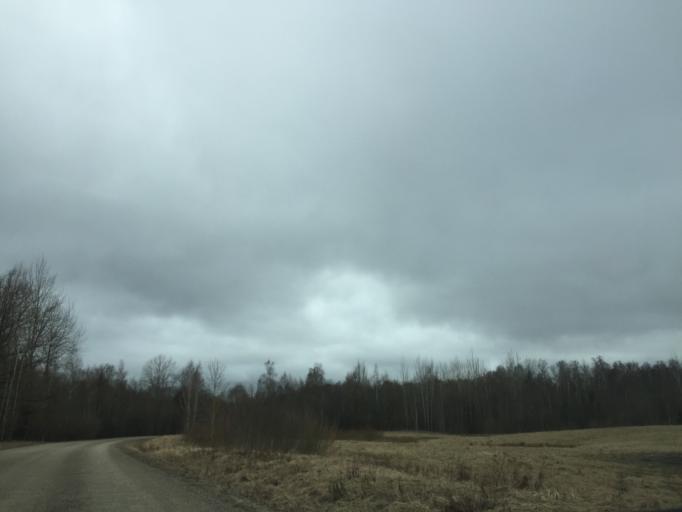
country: LV
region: Ilukste
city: Ilukste
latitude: 56.0225
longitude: 26.2310
